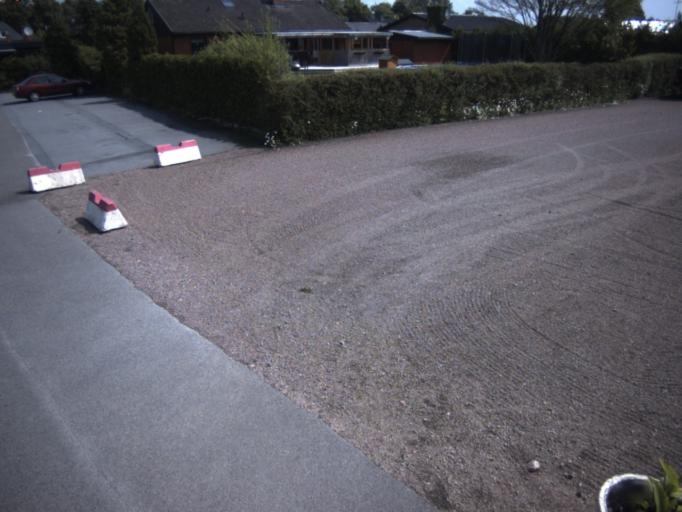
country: SE
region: Skane
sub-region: Angelholms Kommun
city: Strovelstorp
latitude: 56.1384
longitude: 12.8143
